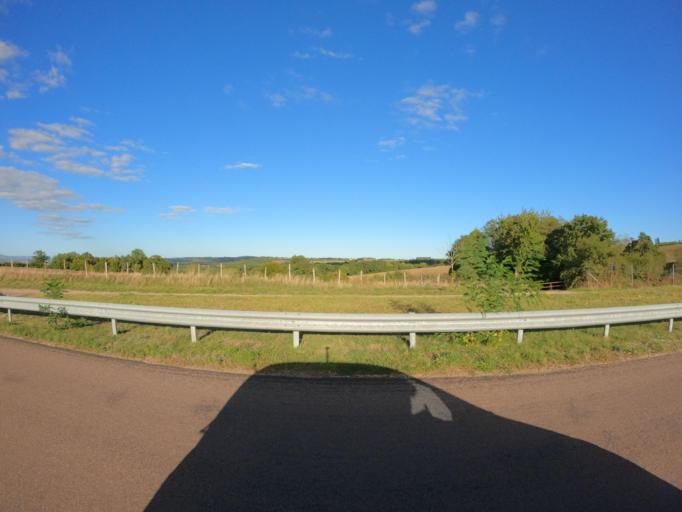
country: FR
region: Bourgogne
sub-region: Departement de Saone-et-Loire
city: Ecuisses
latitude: 46.7443
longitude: 4.5455
